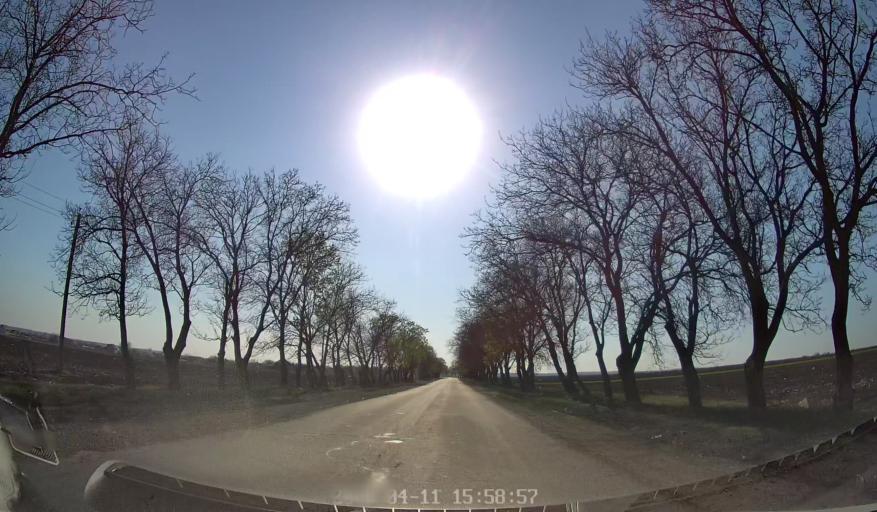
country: MD
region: Chisinau
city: Vadul lui Voda
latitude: 47.0837
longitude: 29.1485
